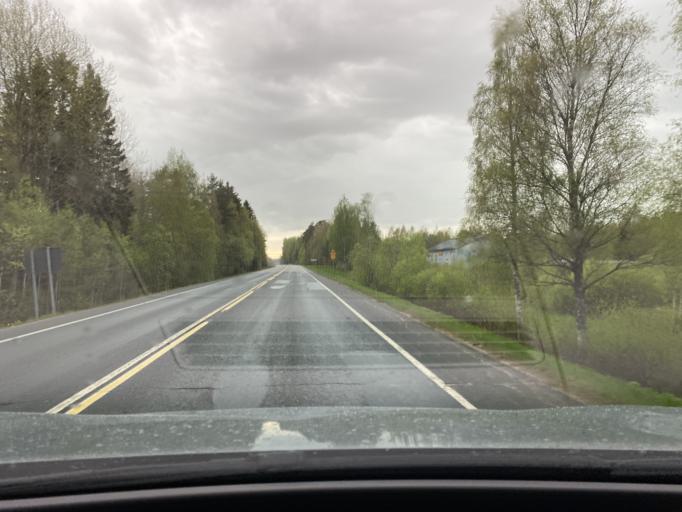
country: FI
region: Varsinais-Suomi
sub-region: Salo
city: Suomusjaervi
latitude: 60.3762
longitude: 23.6084
